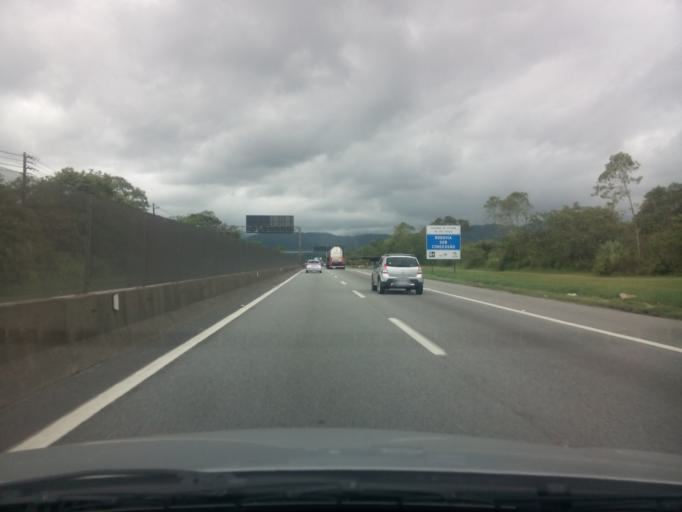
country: BR
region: Sao Paulo
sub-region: Santos
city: Santos
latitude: -23.9082
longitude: -46.2939
